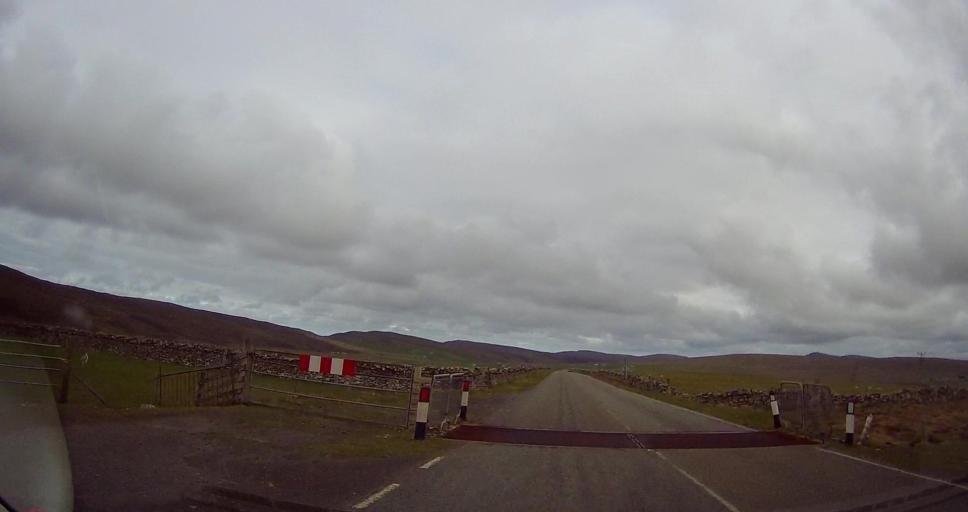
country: GB
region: Scotland
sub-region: Shetland Islands
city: Shetland
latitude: 60.7443
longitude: -0.8840
